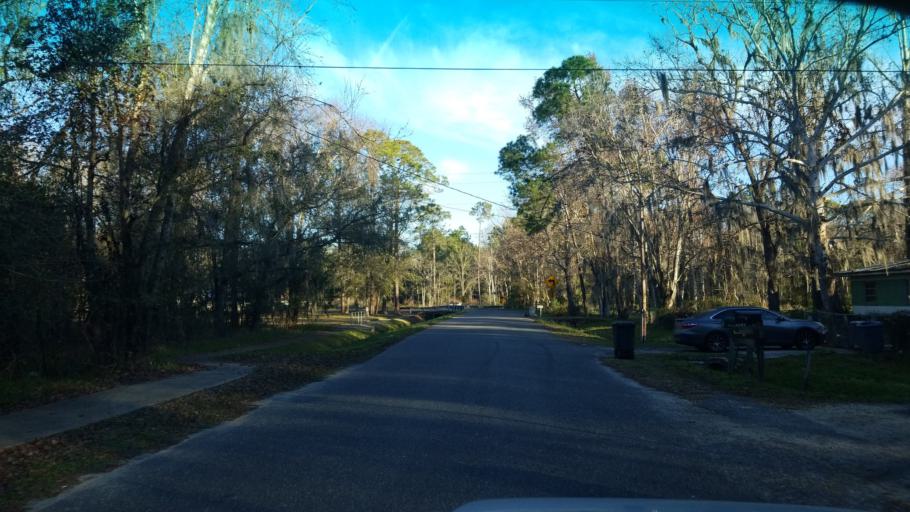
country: US
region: Florida
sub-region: Duval County
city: Baldwin
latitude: 30.3225
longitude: -81.8444
